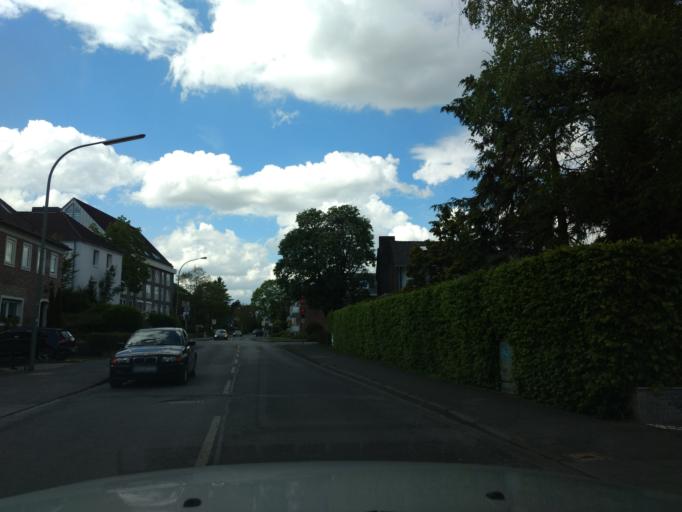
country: DE
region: North Rhine-Westphalia
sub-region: Regierungsbezirk Dusseldorf
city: Meerbusch
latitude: 51.2526
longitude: 6.6957
